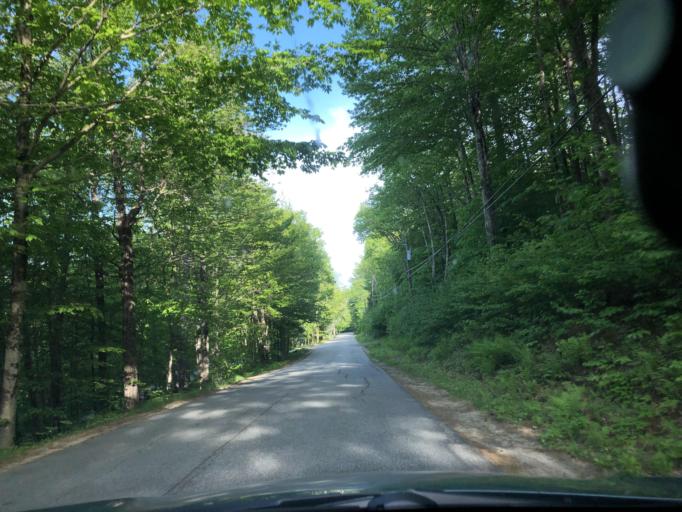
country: US
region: New Hampshire
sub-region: Merrimack County
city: New London
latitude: 43.4237
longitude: -71.9641
